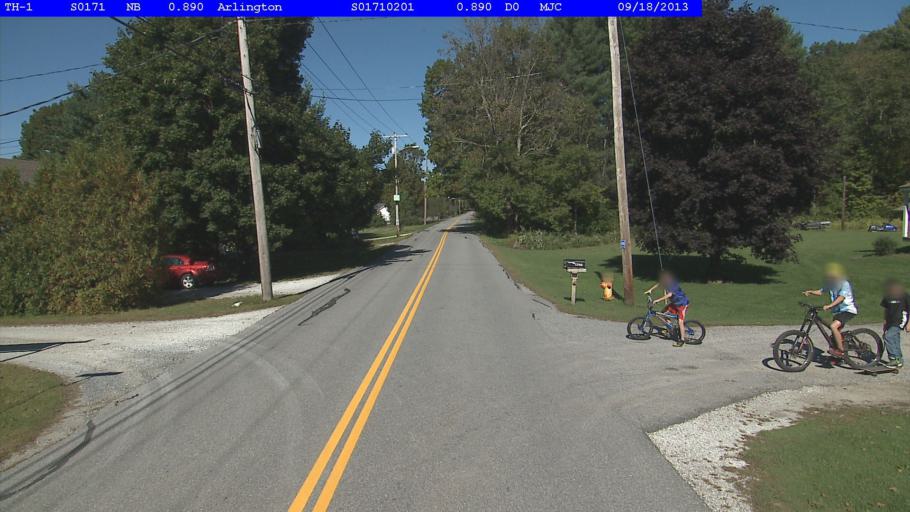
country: US
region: Vermont
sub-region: Bennington County
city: Arlington
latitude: 43.0656
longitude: -73.1406
